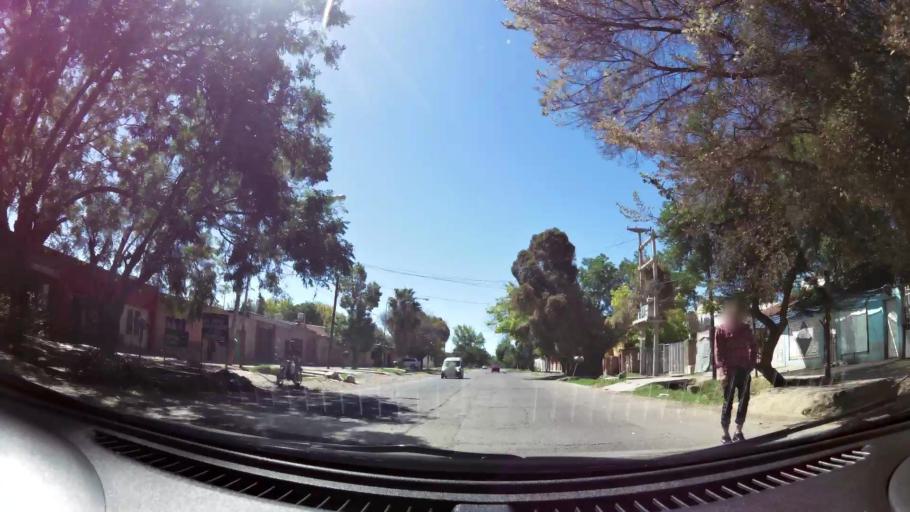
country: AR
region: Mendoza
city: Las Heras
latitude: -32.8384
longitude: -68.8336
